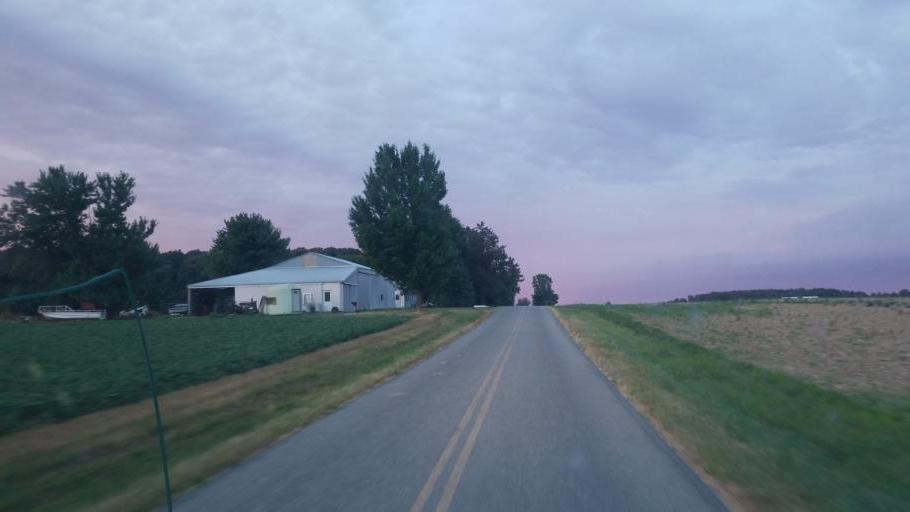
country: US
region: Ohio
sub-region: Defiance County
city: Hicksville
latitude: 41.3343
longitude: -84.8041
